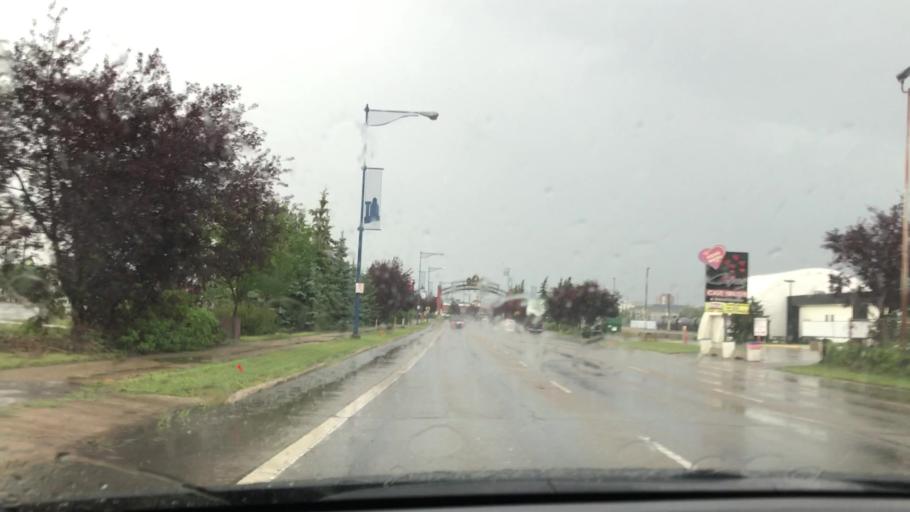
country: CA
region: Alberta
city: Edmonton
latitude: 53.5095
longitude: -113.4942
